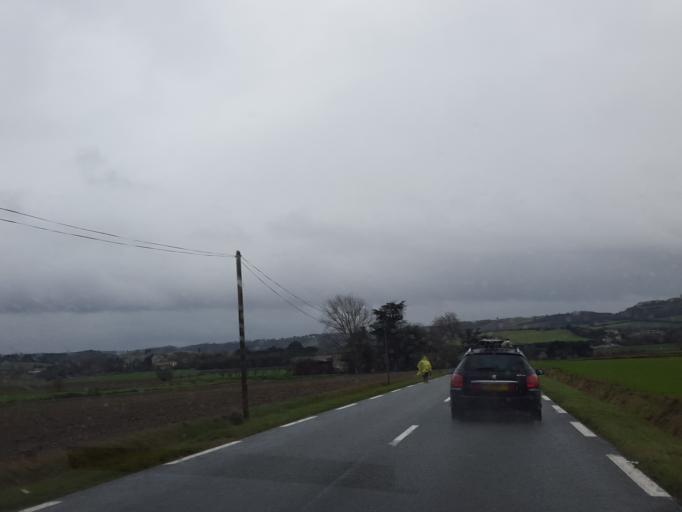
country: FR
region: Languedoc-Roussillon
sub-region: Departement de l'Aude
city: Bram
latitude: 43.2053
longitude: 2.0630
